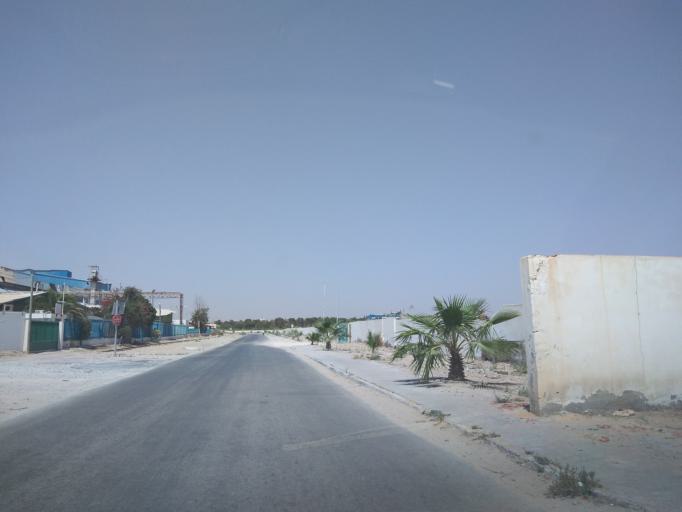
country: TN
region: Safaqis
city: Al Qarmadah
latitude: 34.7304
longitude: 10.7783
